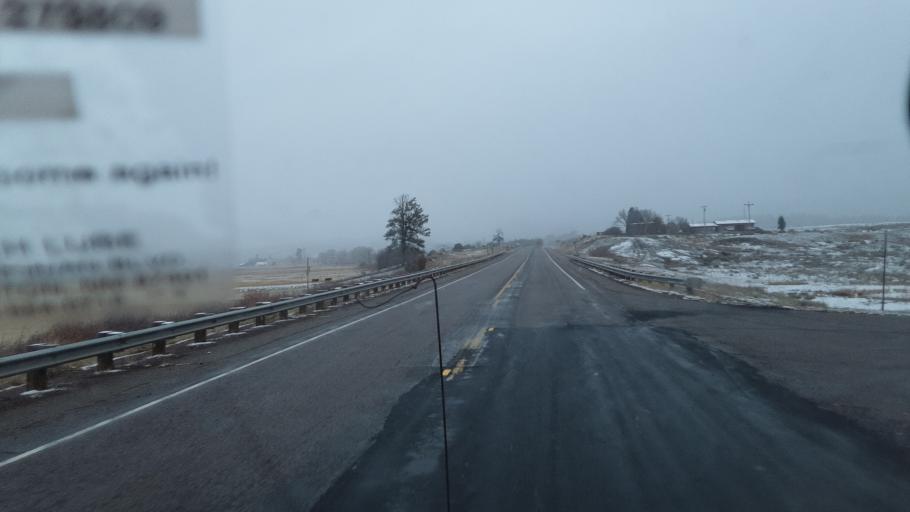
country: US
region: New Mexico
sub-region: Rio Arriba County
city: Tierra Amarilla
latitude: 36.7544
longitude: -106.5617
